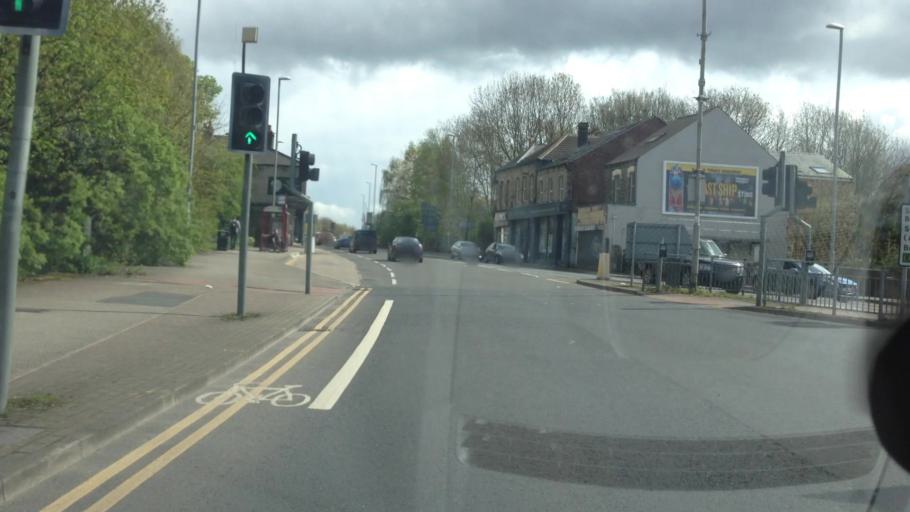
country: GB
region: England
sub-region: City and Borough of Leeds
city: Horsforth
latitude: 53.8156
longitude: -1.6019
